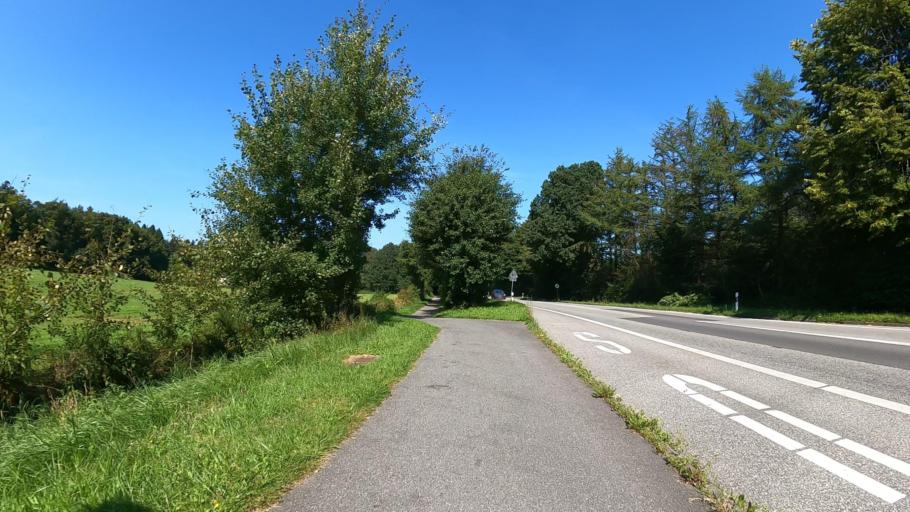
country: DE
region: Schleswig-Holstein
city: Bad Bramstedt
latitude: 53.9015
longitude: 9.8831
